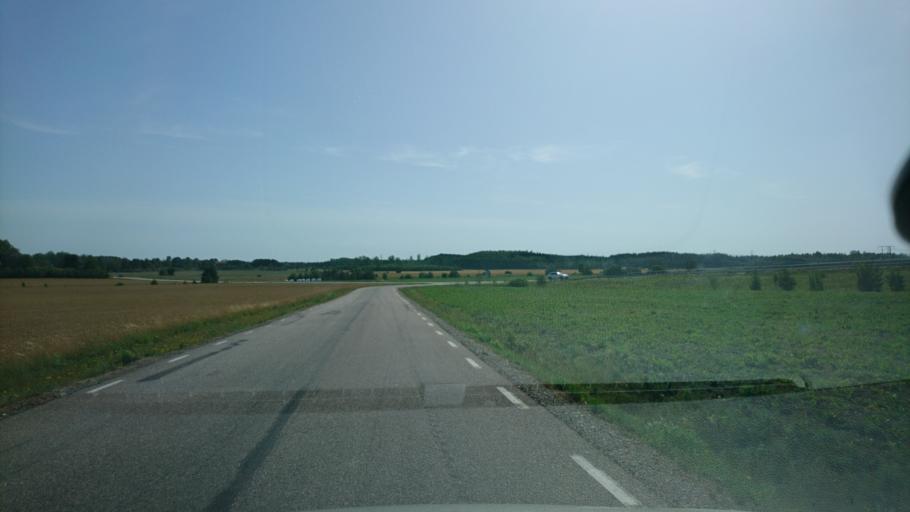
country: SE
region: Soedermanland
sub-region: Strangnas Kommun
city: Strangnas
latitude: 59.3365
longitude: 17.0684
